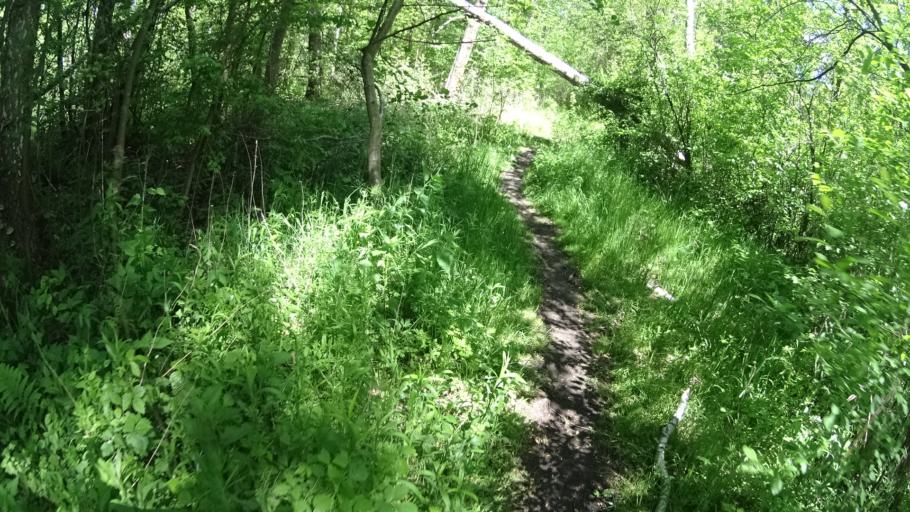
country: PL
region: Masovian Voivodeship
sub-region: Warszawa
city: Bemowo
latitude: 52.2695
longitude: 20.8830
